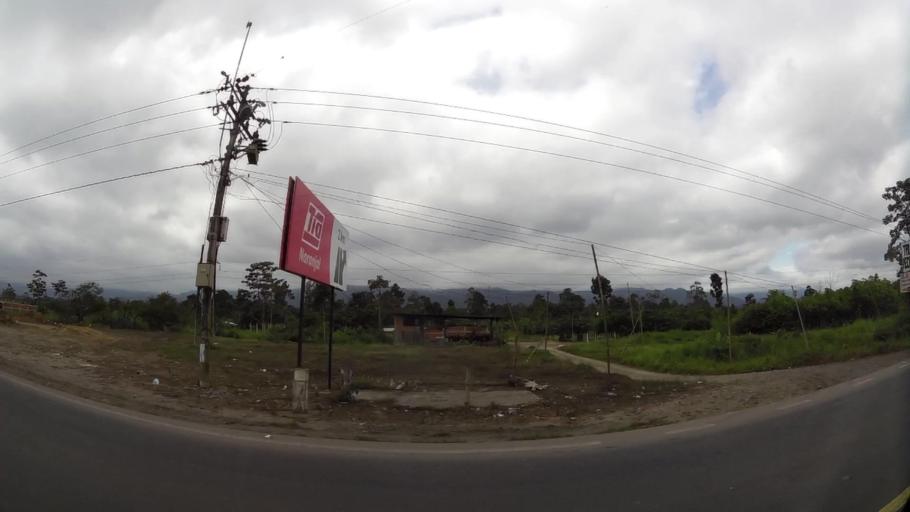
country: EC
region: Guayas
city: Naranjal
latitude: -2.6856
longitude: -79.6306
